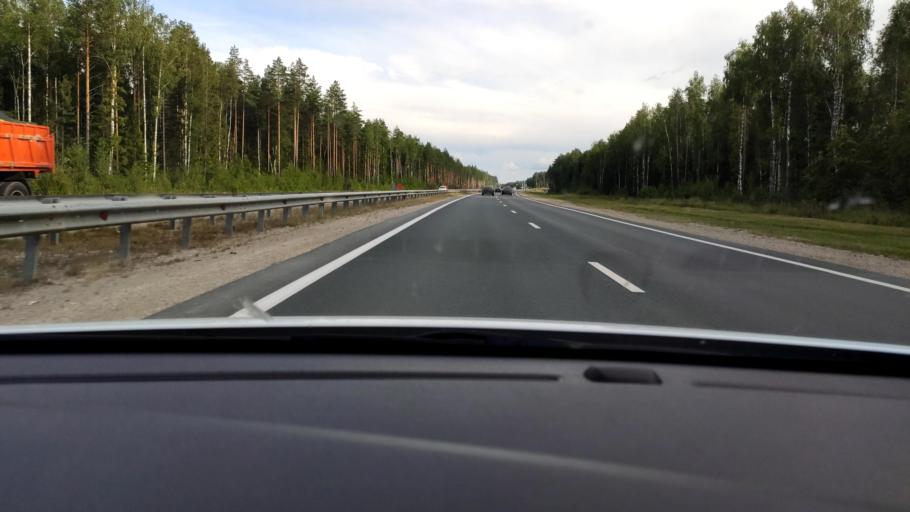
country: RU
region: Mariy-El
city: Surok
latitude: 56.5237
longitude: 48.0087
